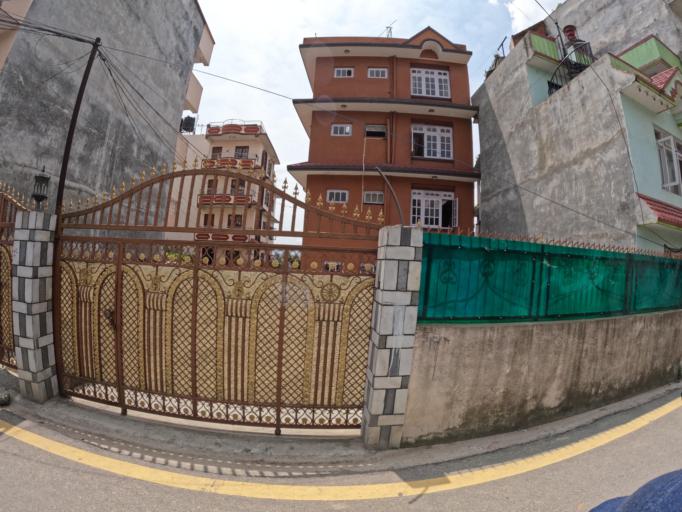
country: NP
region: Central Region
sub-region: Bagmati Zone
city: Kathmandu
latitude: 27.6812
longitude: 85.3722
